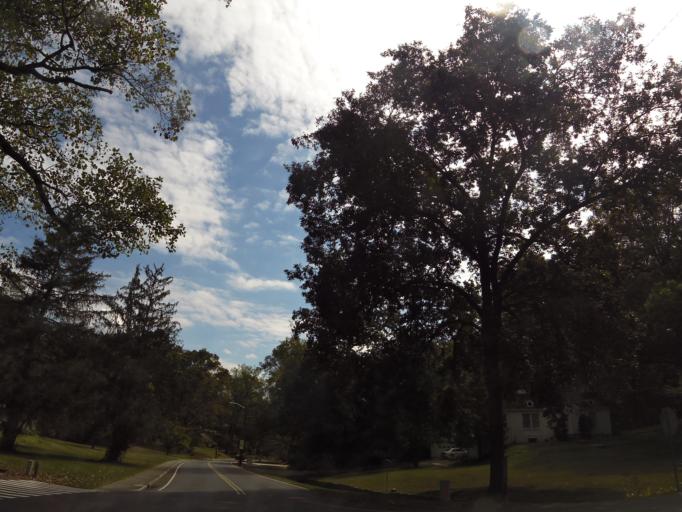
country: US
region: Tennessee
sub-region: Knox County
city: Knoxville
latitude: 35.9981
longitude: -83.8489
